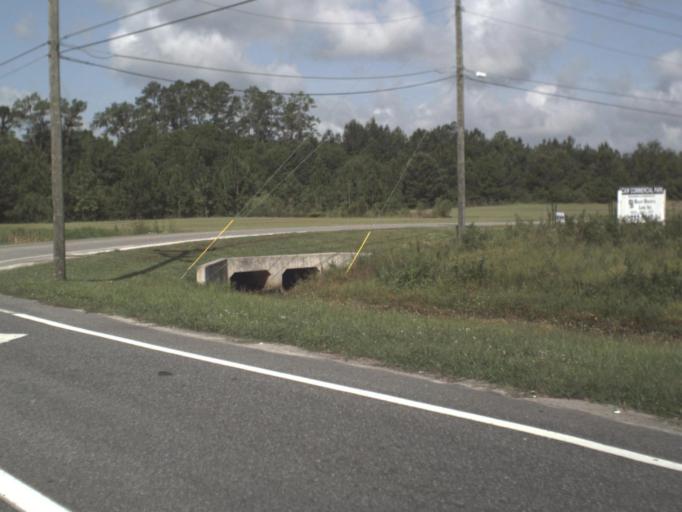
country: US
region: Florida
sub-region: Columbia County
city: Lake City
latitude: 30.1686
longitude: -82.6772
